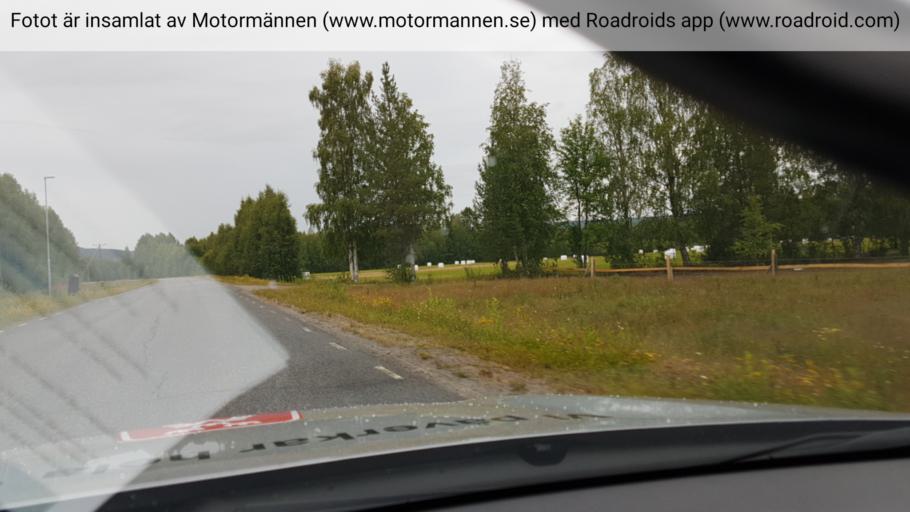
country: SE
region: Norrbotten
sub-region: Bodens Kommun
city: Boden
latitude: 65.8429
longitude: 21.4797
